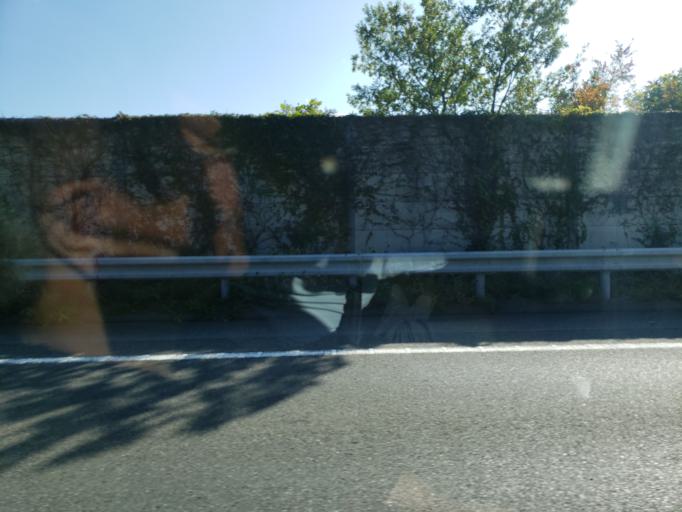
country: JP
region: Hyogo
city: Sumoto
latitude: 34.3510
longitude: 134.8516
